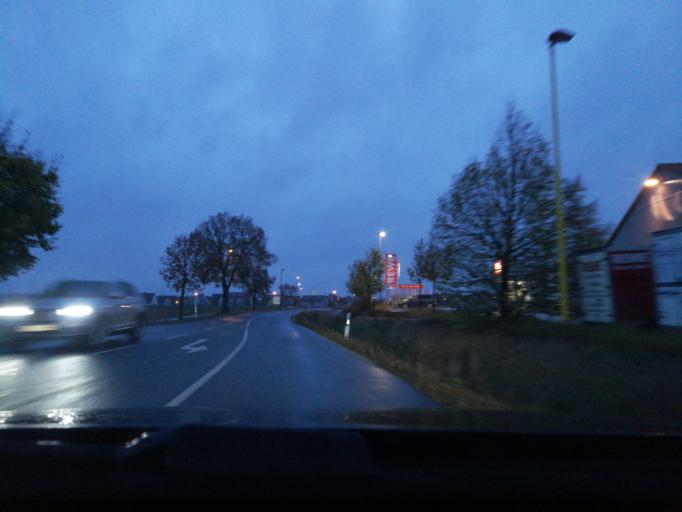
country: DE
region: Bavaria
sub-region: Regierungsbezirk Mittelfranken
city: Obermichelbach
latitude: 49.5242
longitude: 10.9051
